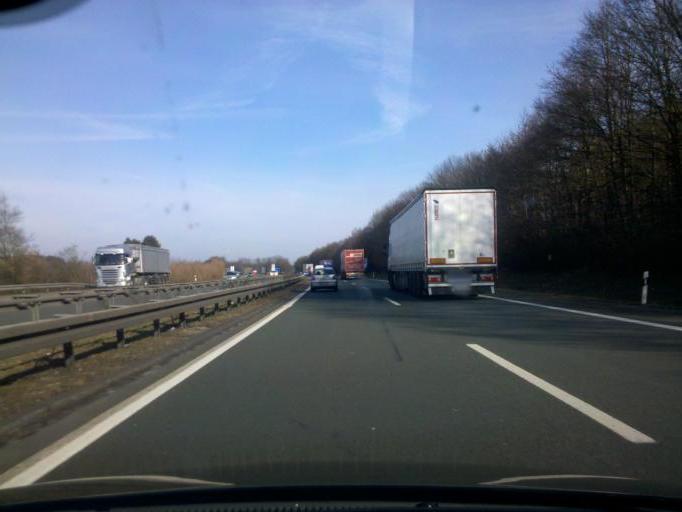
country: DE
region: North Rhine-Westphalia
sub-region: Regierungsbezirk Arnsberg
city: Wilnsdorf
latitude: 50.8098
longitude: 8.0990
